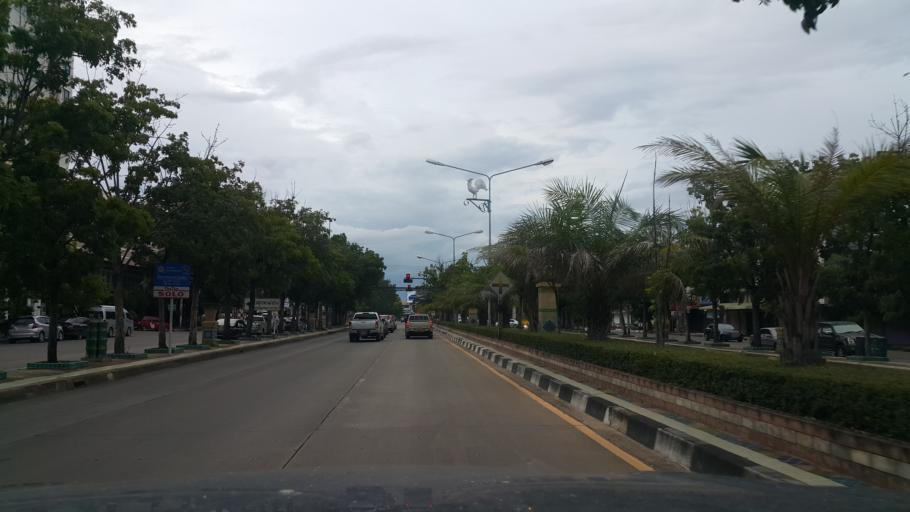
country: TH
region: Lampang
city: Lampang
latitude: 18.2810
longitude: 99.4880
